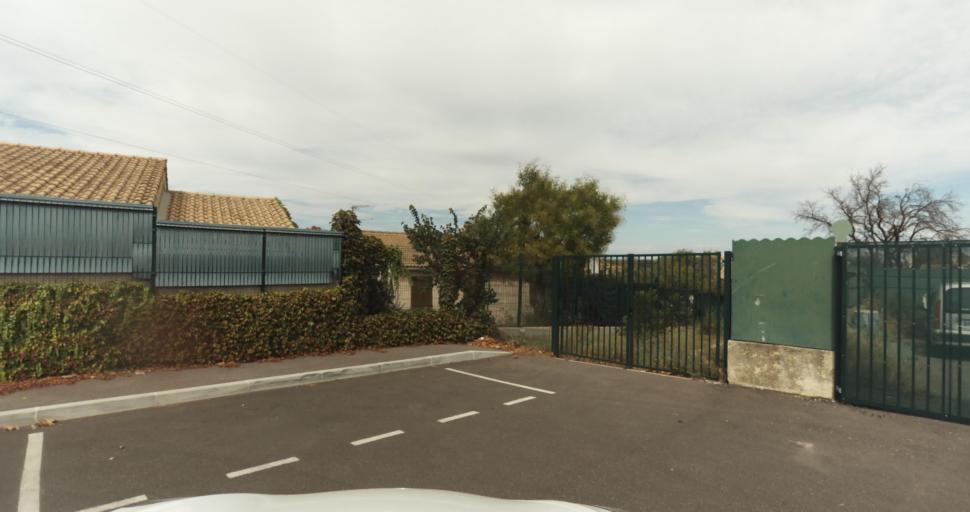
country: FR
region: Provence-Alpes-Cote d'Azur
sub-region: Departement des Bouches-du-Rhone
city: Miramas
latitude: 43.5752
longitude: 5.0096
